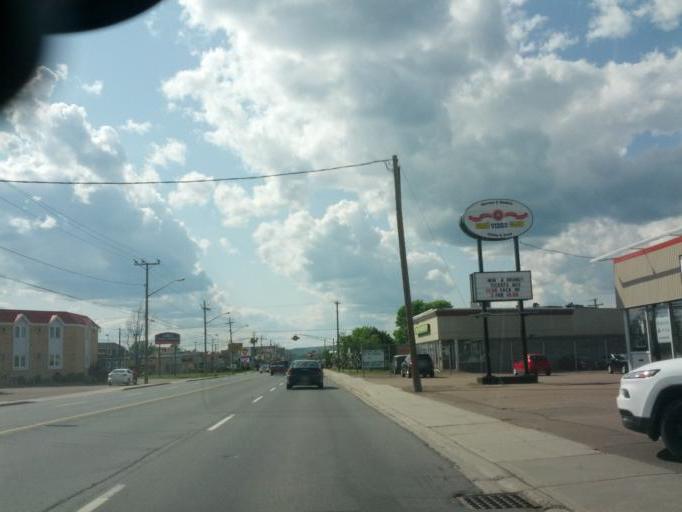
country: CA
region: New Brunswick
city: Moncton
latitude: 46.1044
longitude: -64.8194
